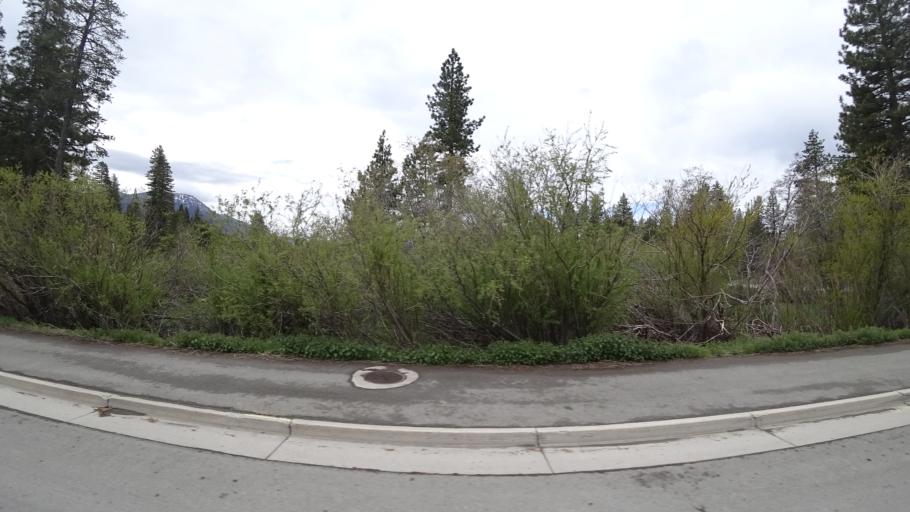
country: US
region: Nevada
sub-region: Washoe County
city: Incline Village
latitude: 39.2490
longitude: -119.9456
